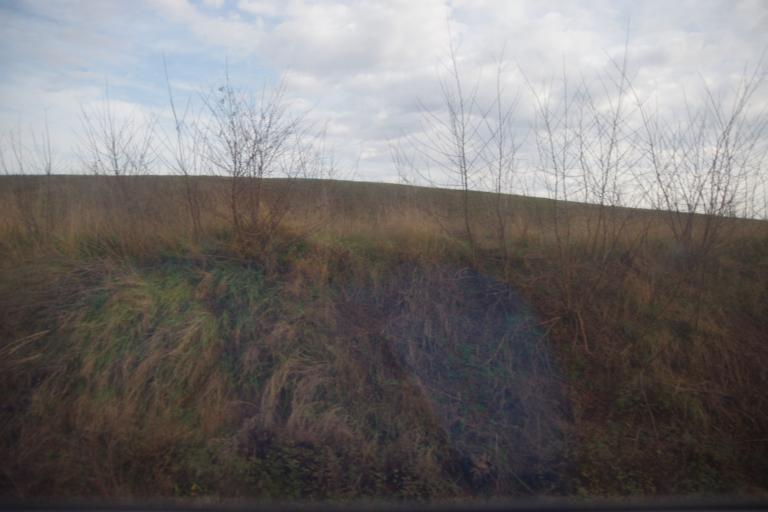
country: RU
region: Krasnodarskiy
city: Saratovskaya
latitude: 44.7979
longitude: 39.2314
